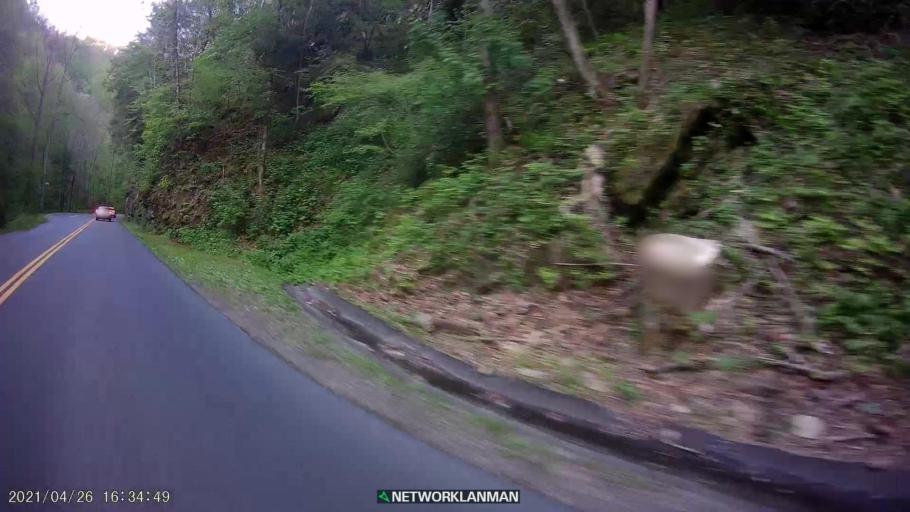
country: US
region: Tennessee
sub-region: Sevier County
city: Pigeon Forge
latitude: 35.6480
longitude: -83.7146
